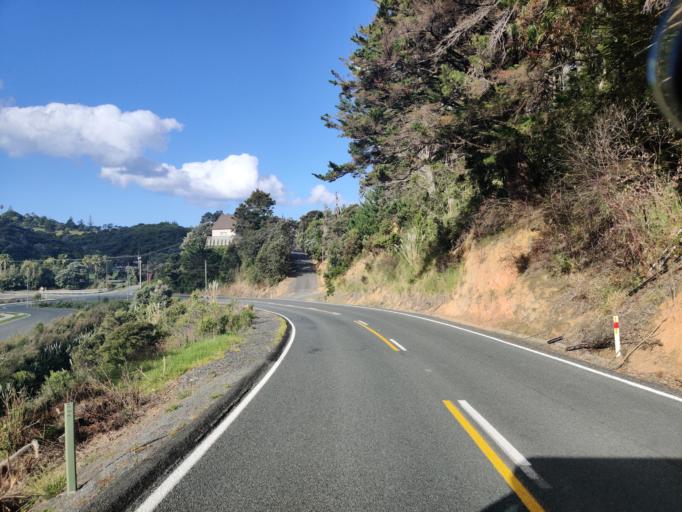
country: NZ
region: Northland
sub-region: Whangarei
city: Ngunguru
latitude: -35.6121
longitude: 174.5238
